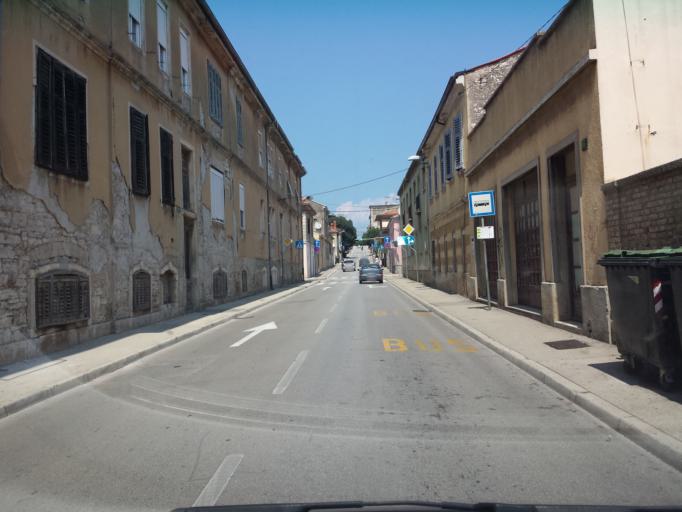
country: HR
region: Istarska
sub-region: Grad Pula
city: Pula
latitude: 44.8686
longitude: 13.8529
